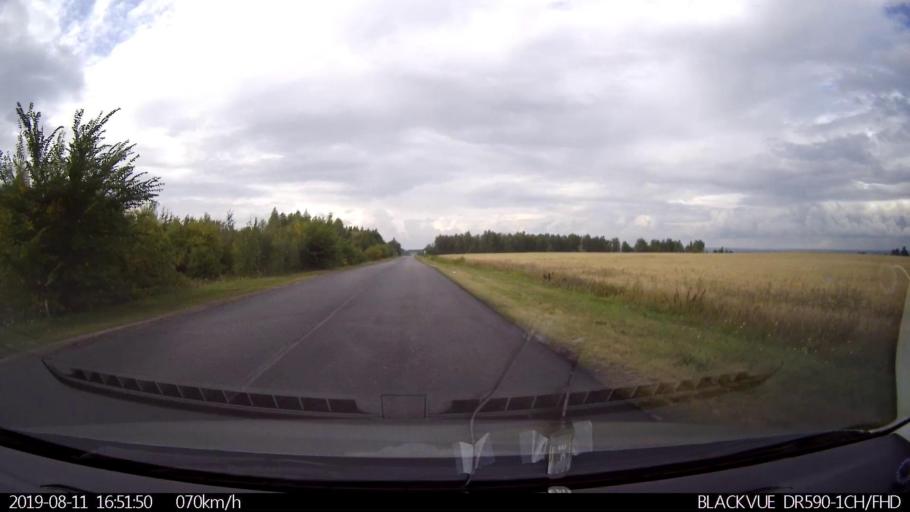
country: RU
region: Ulyanovsk
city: Mayna
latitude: 54.2412
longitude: 47.6759
